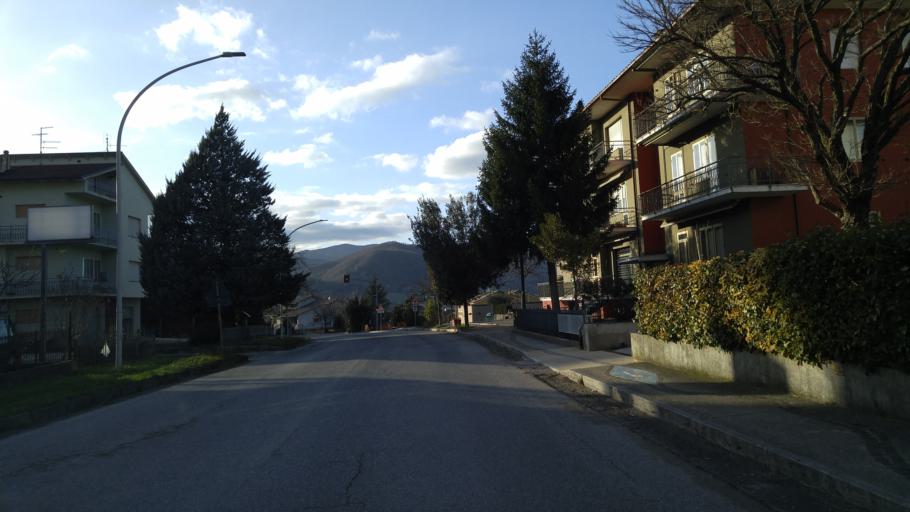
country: IT
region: The Marches
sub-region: Provincia di Pesaro e Urbino
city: Cagli
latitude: 43.5468
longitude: 12.6579
